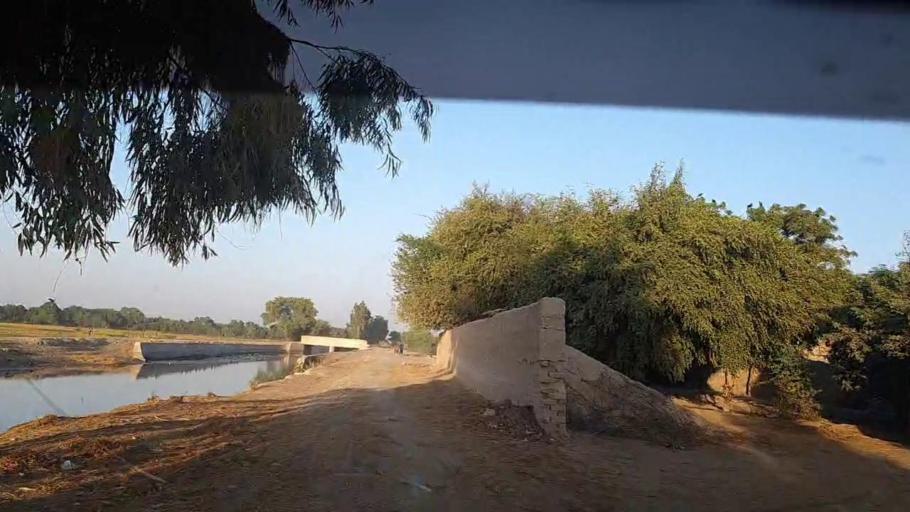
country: PK
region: Sindh
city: Ratodero
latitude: 27.8783
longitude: 68.2026
